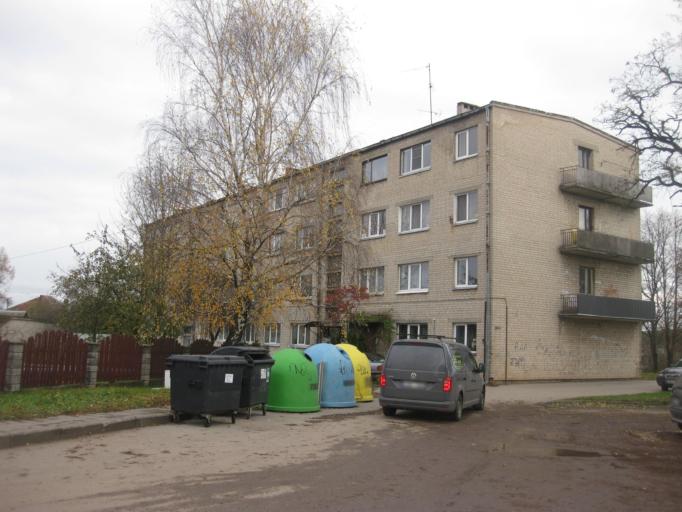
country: LT
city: Prienai
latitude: 54.6324
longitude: 23.9483
